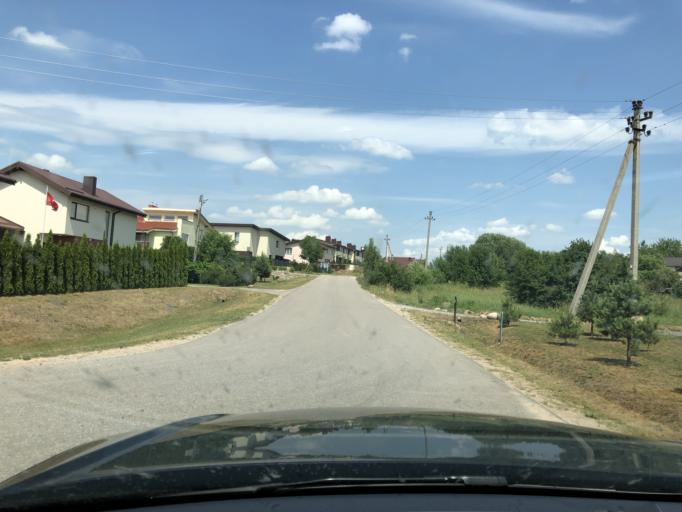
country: LT
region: Vilnius County
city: Pasilaiciai
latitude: 54.7505
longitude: 25.1909
